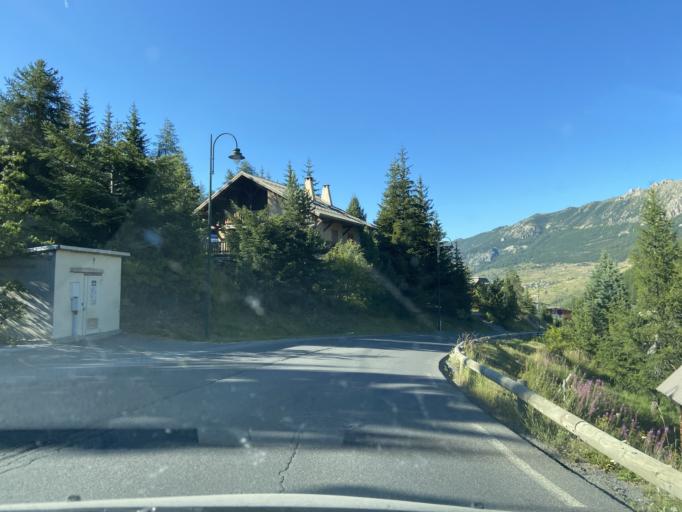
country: FR
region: Provence-Alpes-Cote d'Azur
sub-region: Departement des Hautes-Alpes
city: Guillestre
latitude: 44.5762
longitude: 6.6820
